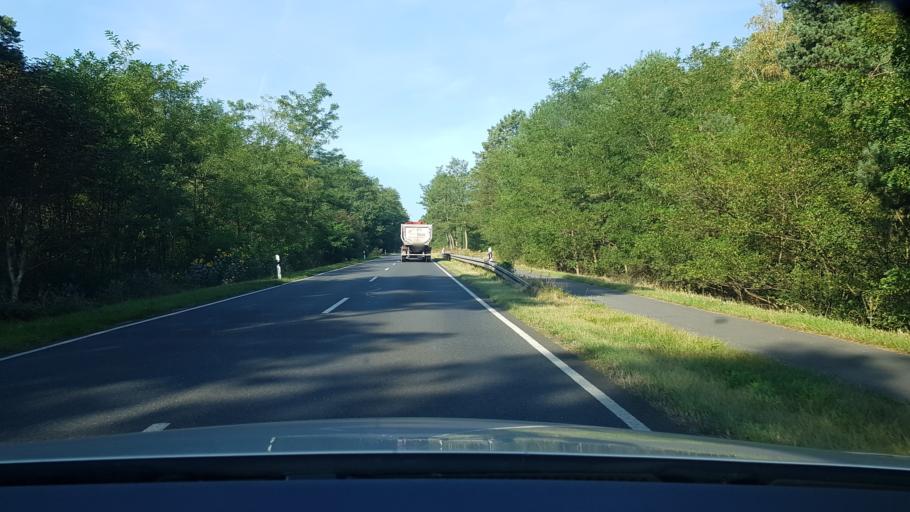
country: DE
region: Brandenburg
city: Eisenhuettenstadt
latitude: 52.1517
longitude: 14.5930
